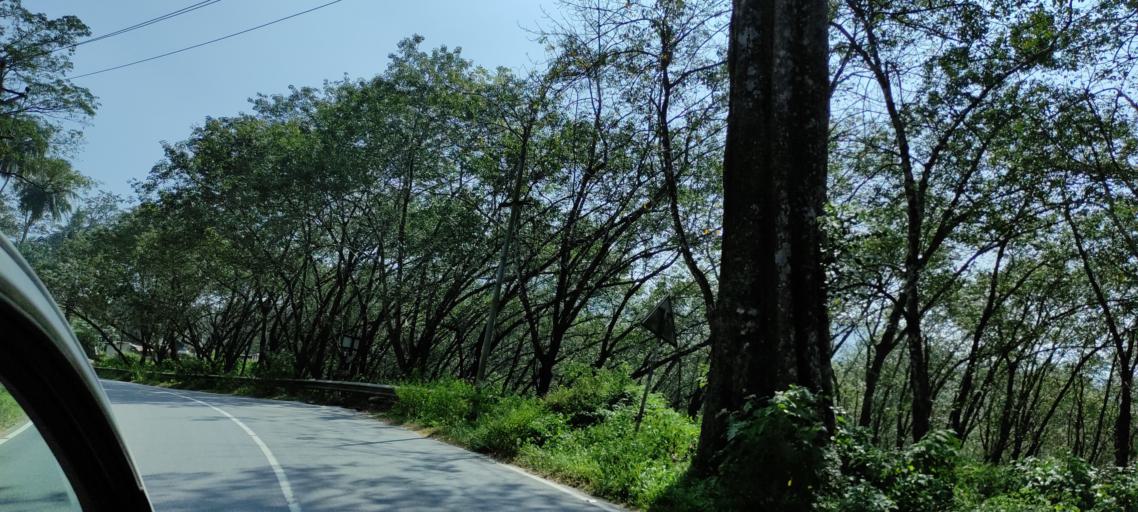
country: IN
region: Kerala
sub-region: Kollam
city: Punalur
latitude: 8.9732
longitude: 77.0657
